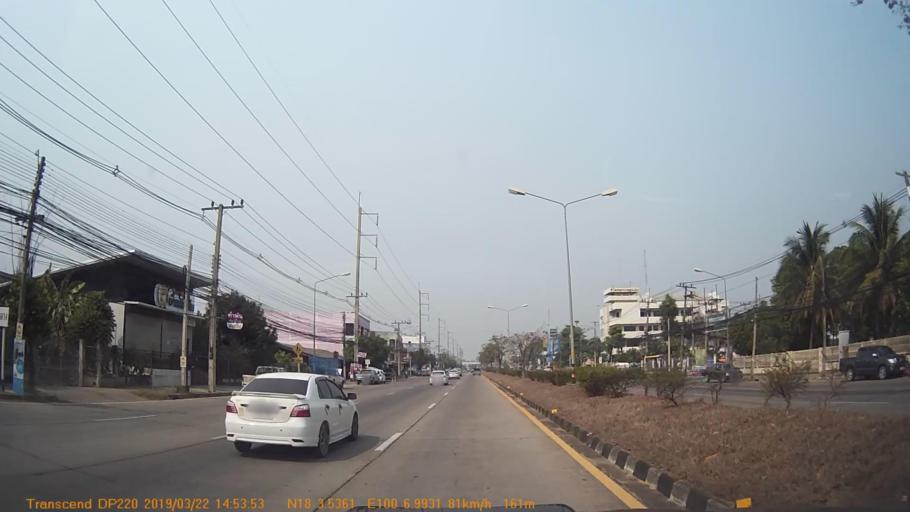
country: TH
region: Phrae
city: Sung Men
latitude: 18.0593
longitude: 100.1167
